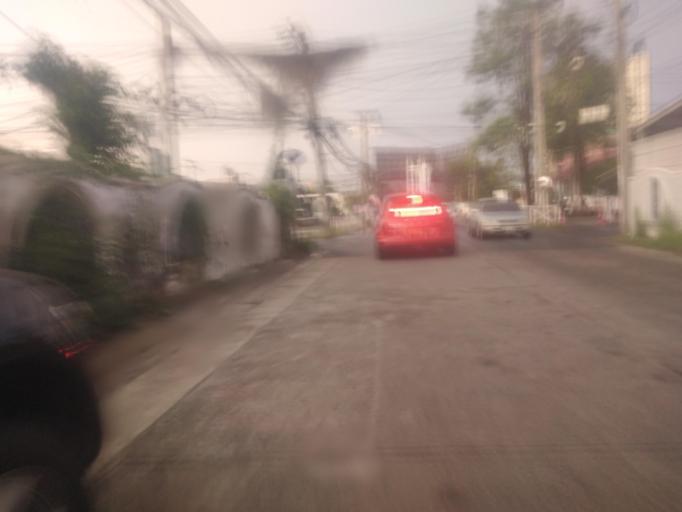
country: TH
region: Bangkok
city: Phasi Charoen
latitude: 13.7418
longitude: 100.4458
